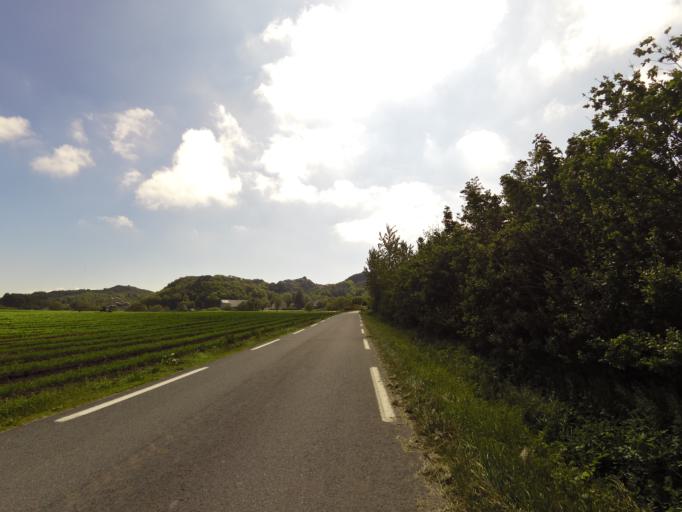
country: NO
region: Rogaland
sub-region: Ha
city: Vigrestad
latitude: 58.5182
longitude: 5.8182
